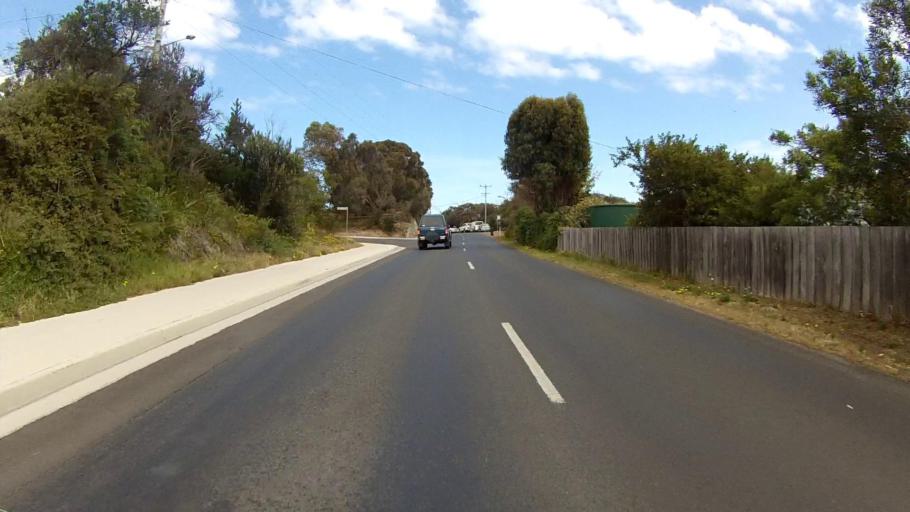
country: AU
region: Tasmania
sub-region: Sorell
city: Sorell
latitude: -42.8616
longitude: 147.6124
